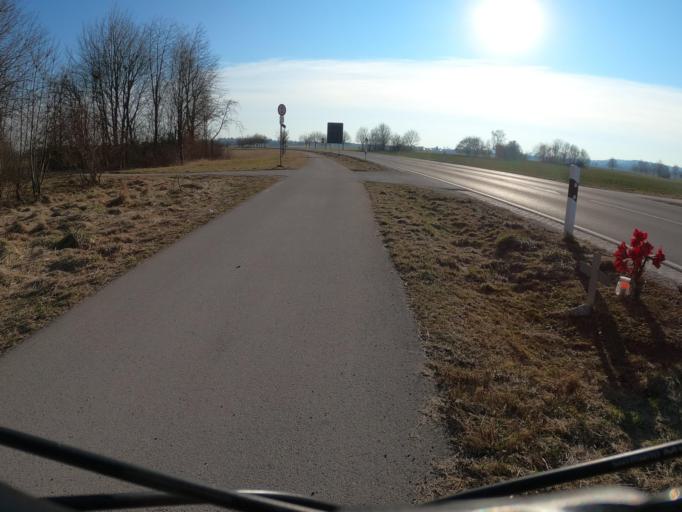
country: DE
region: Bavaria
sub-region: Swabia
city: Neu-Ulm
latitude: 48.4223
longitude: 10.0579
